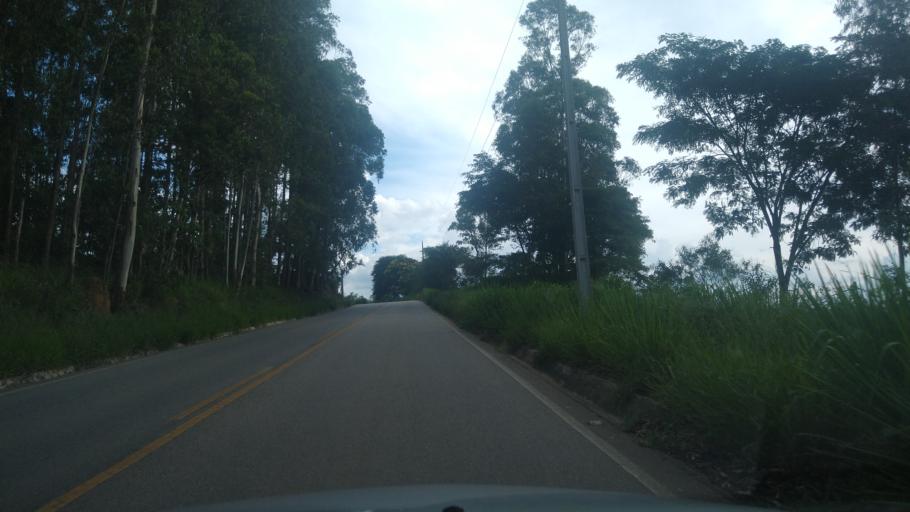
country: BR
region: Minas Gerais
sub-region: Extrema
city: Extrema
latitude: -22.7957
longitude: -46.3168
